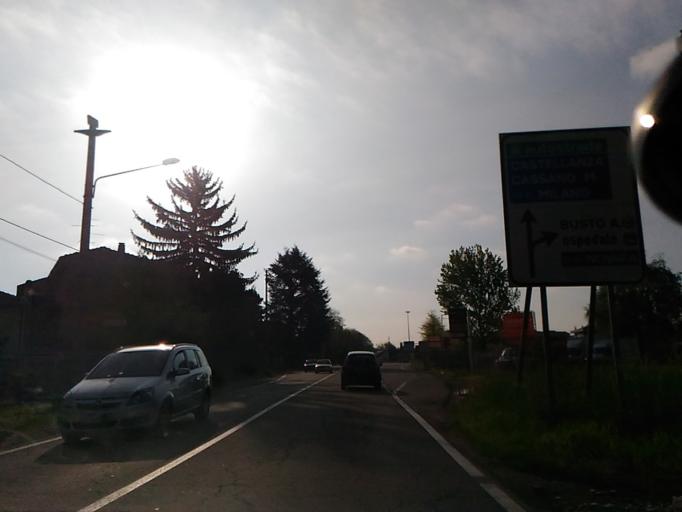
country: IT
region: Lombardy
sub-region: Provincia di Varese
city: Busto Arsizio
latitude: 45.6266
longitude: 8.8467
